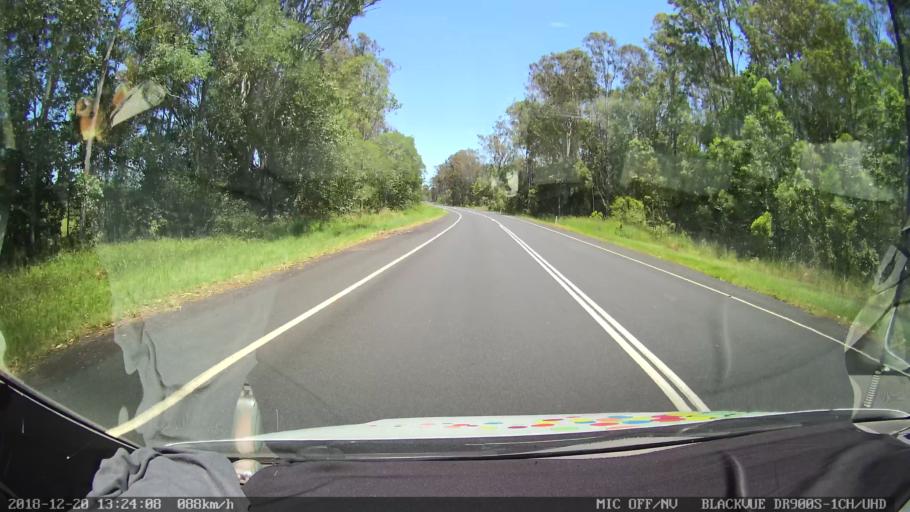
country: AU
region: New South Wales
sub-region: Richmond Valley
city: Casino
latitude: -29.1134
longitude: 153.0005
